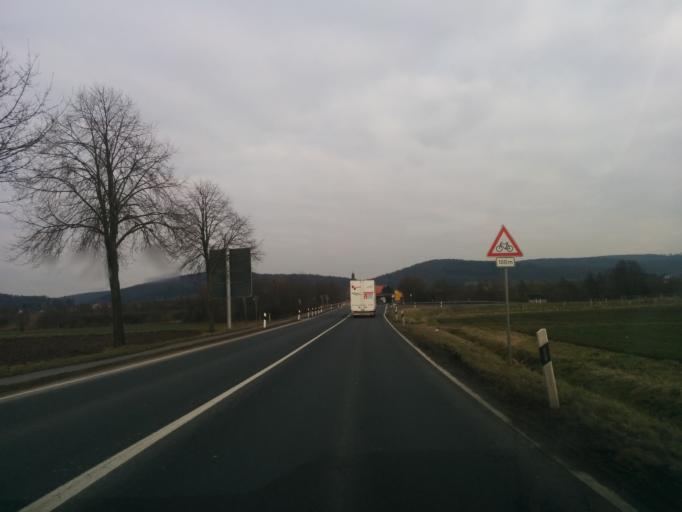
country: DE
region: Lower Saxony
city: Norten-Hardenberg
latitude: 51.6282
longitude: 9.9229
